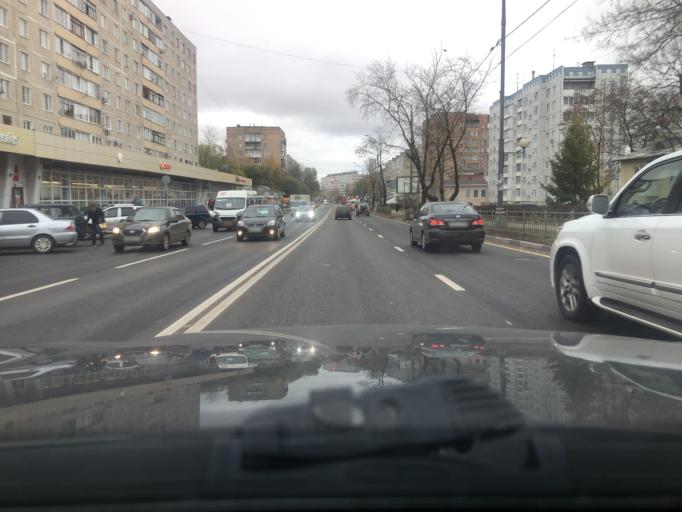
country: RU
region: Moskovskaya
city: Sergiyev Posad
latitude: 56.3269
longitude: 38.1326
